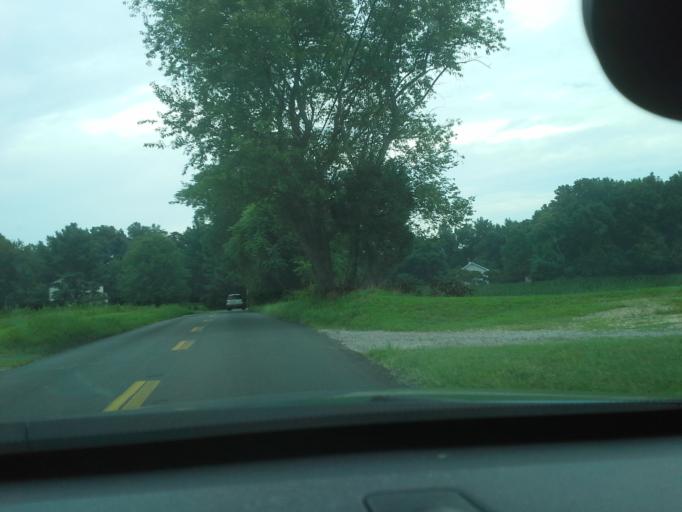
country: US
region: Maryland
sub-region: Calvert County
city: Dunkirk Town Center
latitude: 38.7465
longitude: -76.6408
